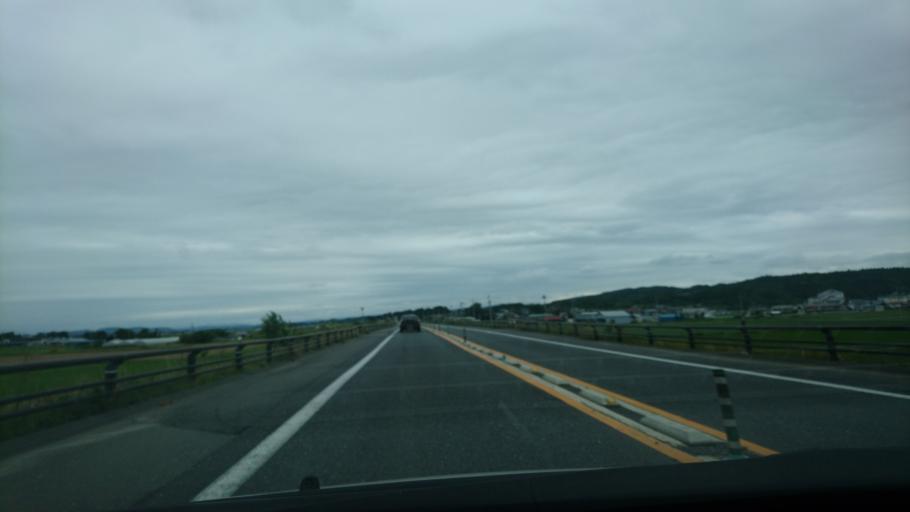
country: JP
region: Miyagi
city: Wakuya
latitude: 38.6577
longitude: 141.2646
